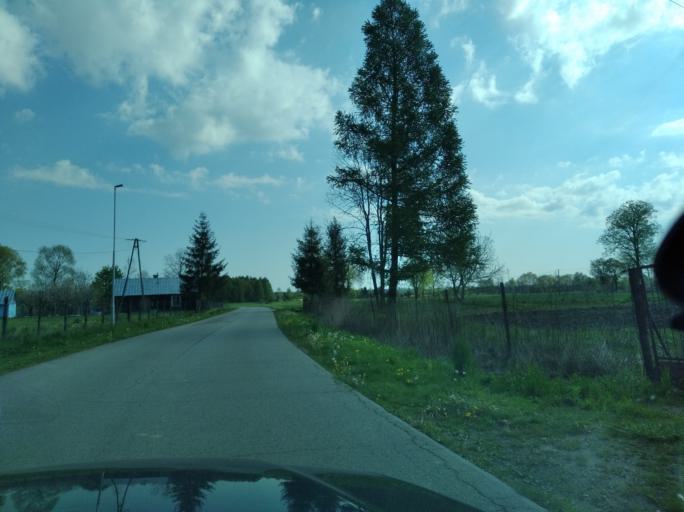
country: PL
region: Subcarpathian Voivodeship
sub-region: Powiat lubaczowski
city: Wielkie Oczy
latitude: 49.9751
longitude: 23.0614
